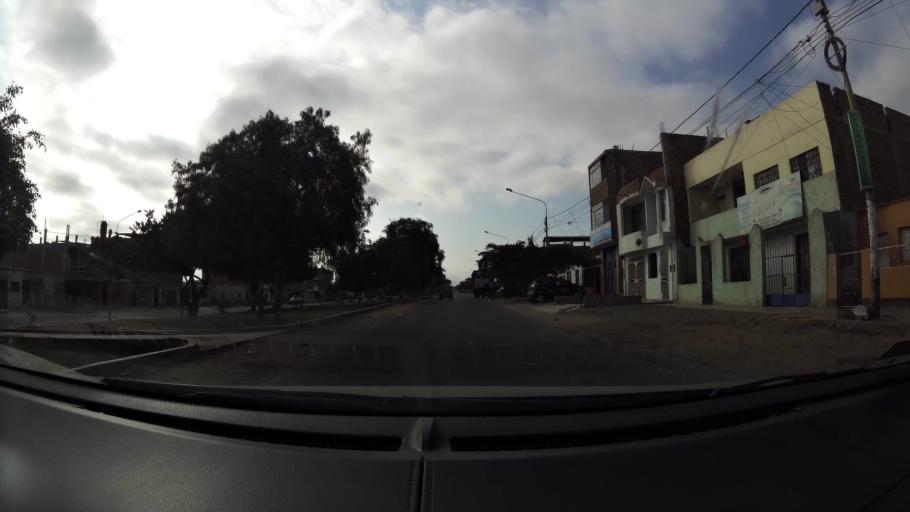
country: PE
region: La Libertad
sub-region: Provincia de Trujillo
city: La Esperanza
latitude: -8.0771
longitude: -79.0447
